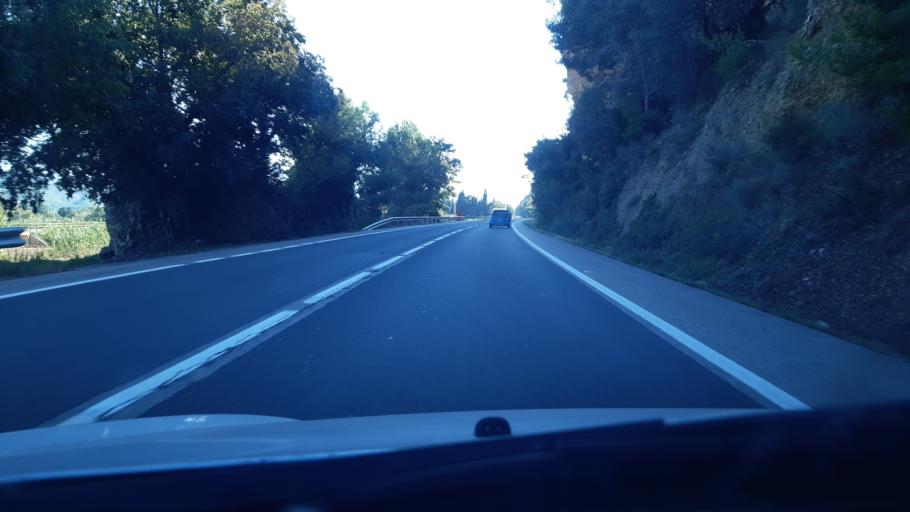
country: ES
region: Catalonia
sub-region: Provincia de Tarragona
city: Tivenys
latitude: 40.8685
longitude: 0.5034
